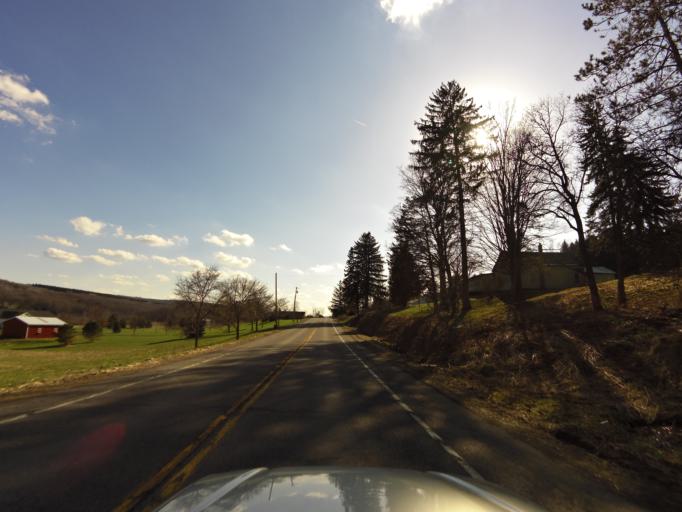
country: US
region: New York
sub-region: Cattaraugus County
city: Franklinville
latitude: 42.3913
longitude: -78.3704
